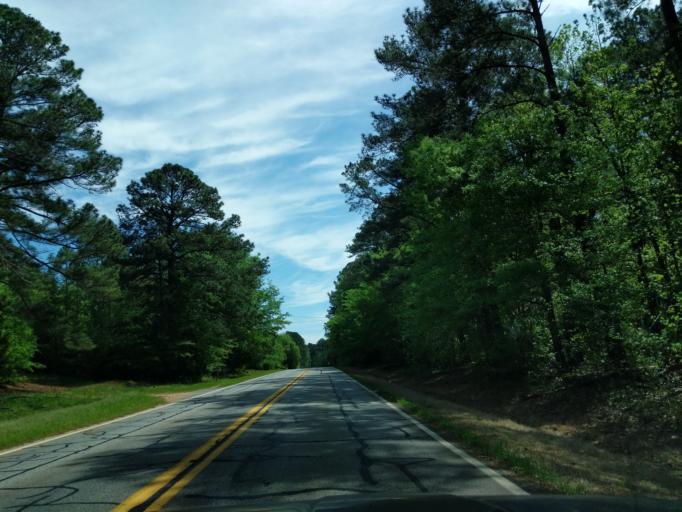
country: US
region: Georgia
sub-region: Columbia County
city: Appling
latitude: 33.6121
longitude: -82.3099
